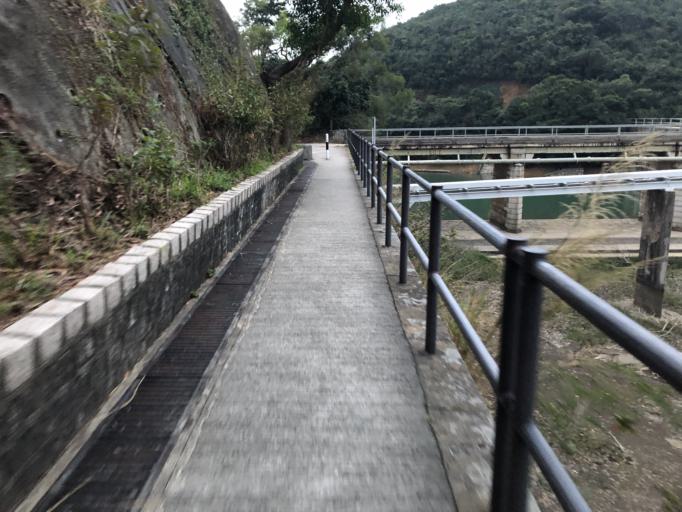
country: HK
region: Wanchai
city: Wan Chai
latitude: 22.2571
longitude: 114.2105
